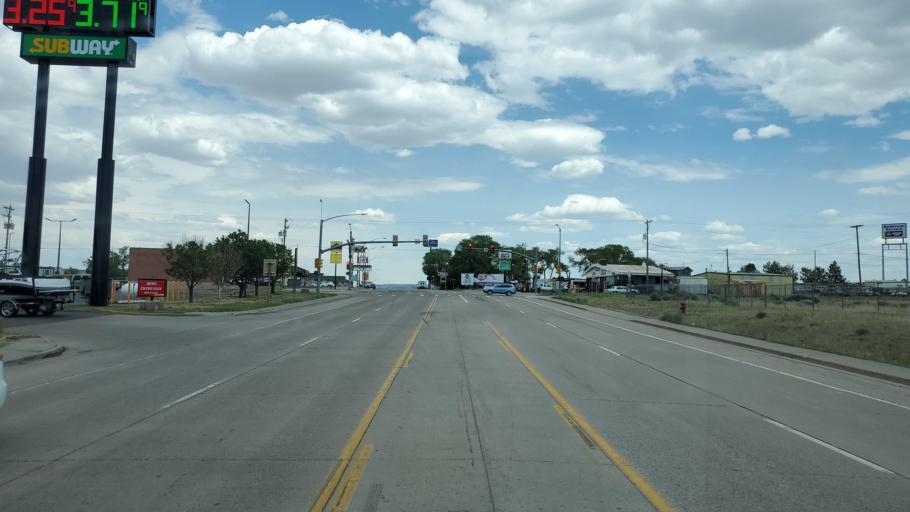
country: US
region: Wyoming
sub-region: Uinta County
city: Evanston
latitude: 41.2641
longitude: -110.9782
